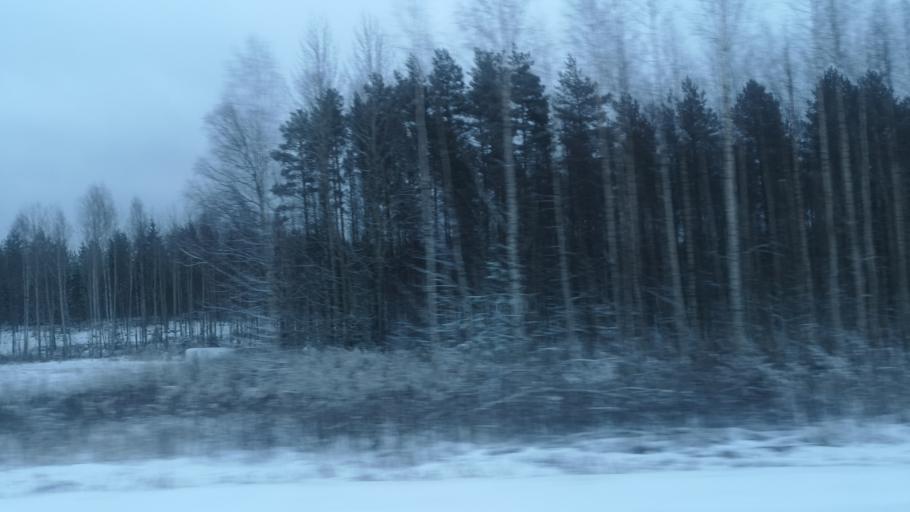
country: FI
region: Southern Savonia
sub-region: Savonlinna
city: Enonkoski
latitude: 62.0496
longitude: 28.7045
